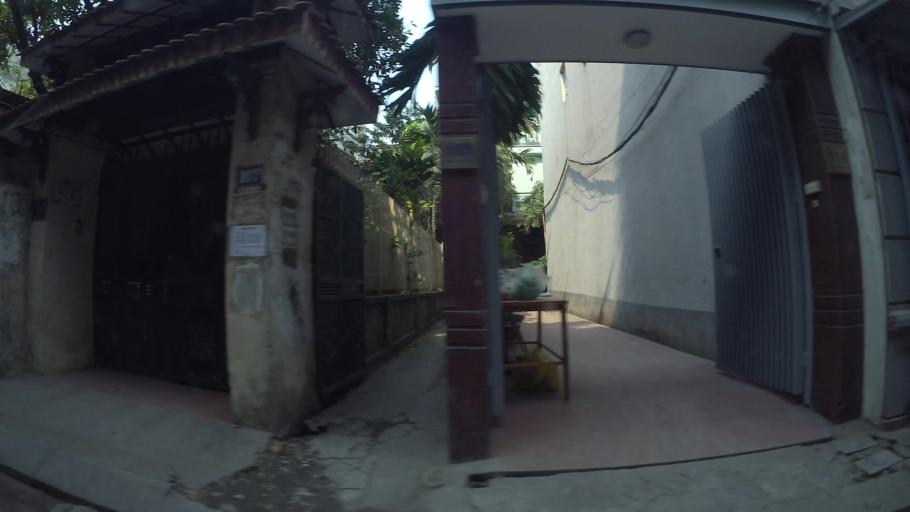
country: VN
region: Ha Noi
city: Thanh Xuan
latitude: 20.9893
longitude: 105.8179
